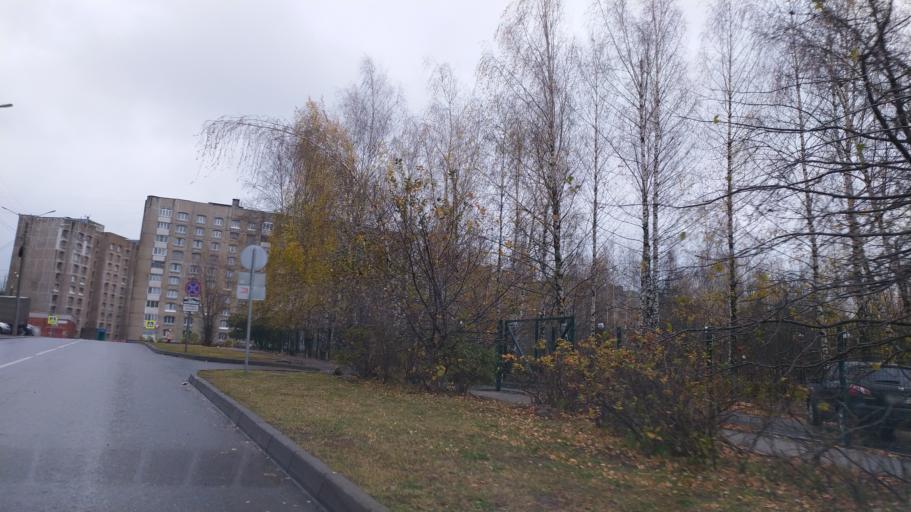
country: RU
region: Chuvashia
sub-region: Cheboksarskiy Rayon
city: Cheboksary
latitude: 56.1427
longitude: 47.1643
